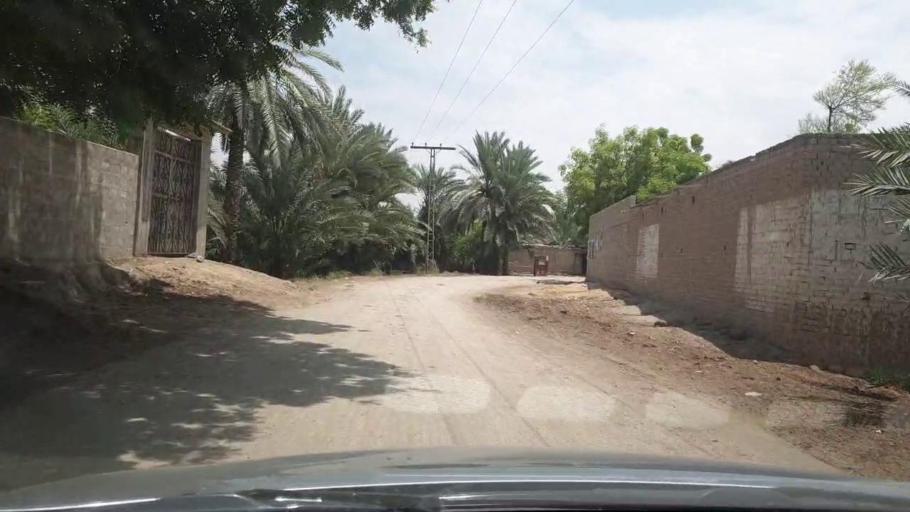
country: PK
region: Sindh
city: Khairpur
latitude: 27.4325
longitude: 68.7704
